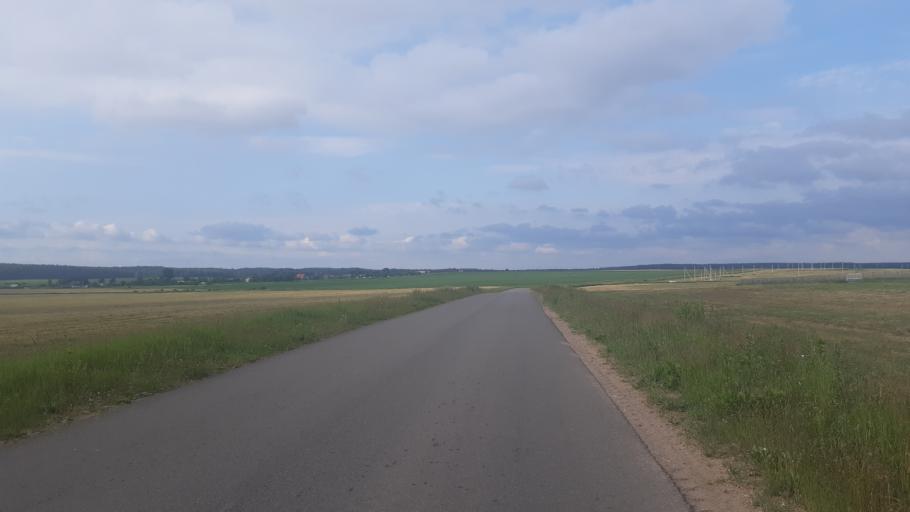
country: BY
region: Minsk
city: Horad Zhodzina
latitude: 54.1433
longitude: 28.2355
